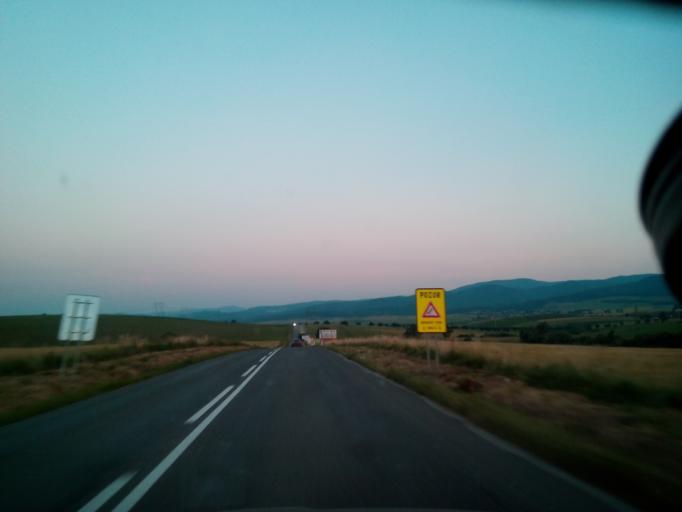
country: SK
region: Kosicky
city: Spisska Nova Ves
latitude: 48.9941
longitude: 20.4729
